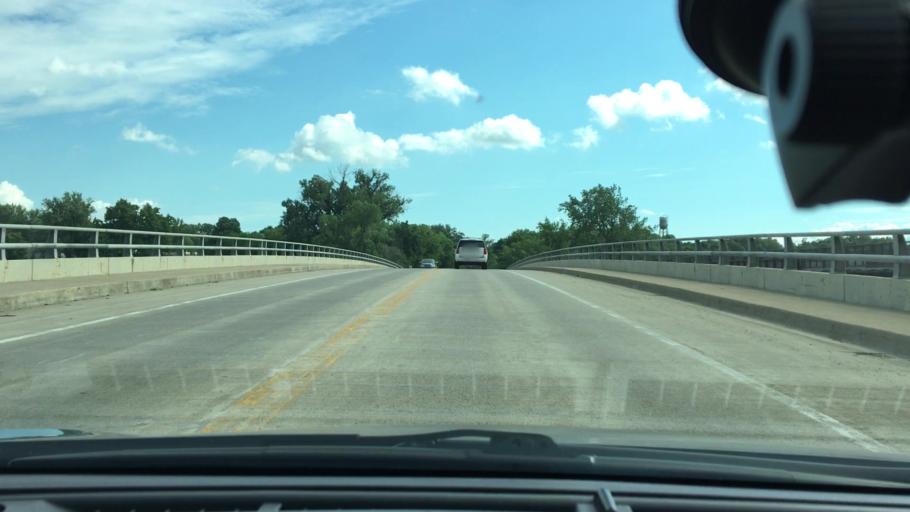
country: US
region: Minnesota
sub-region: Hennepin County
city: Orono
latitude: 44.9449
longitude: -93.5795
